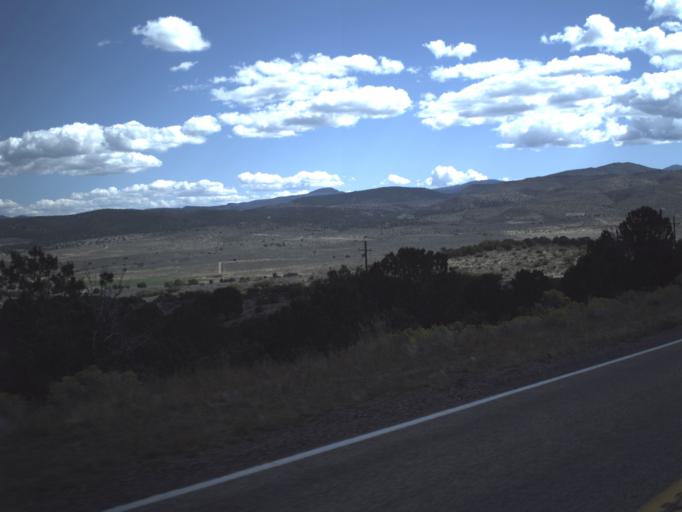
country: US
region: Utah
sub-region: Washington County
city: Enterprise
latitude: 37.5246
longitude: -113.6421
